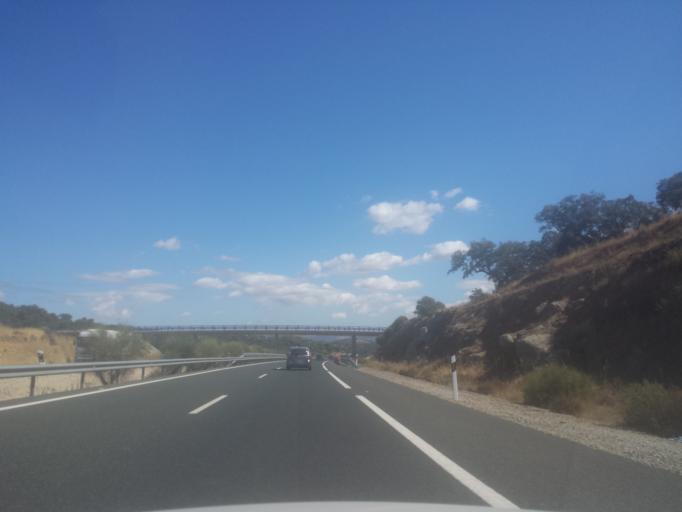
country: ES
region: Andalusia
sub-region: Provincia de Huelva
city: Santa Olalla del Cala
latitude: 37.9290
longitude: -6.2278
